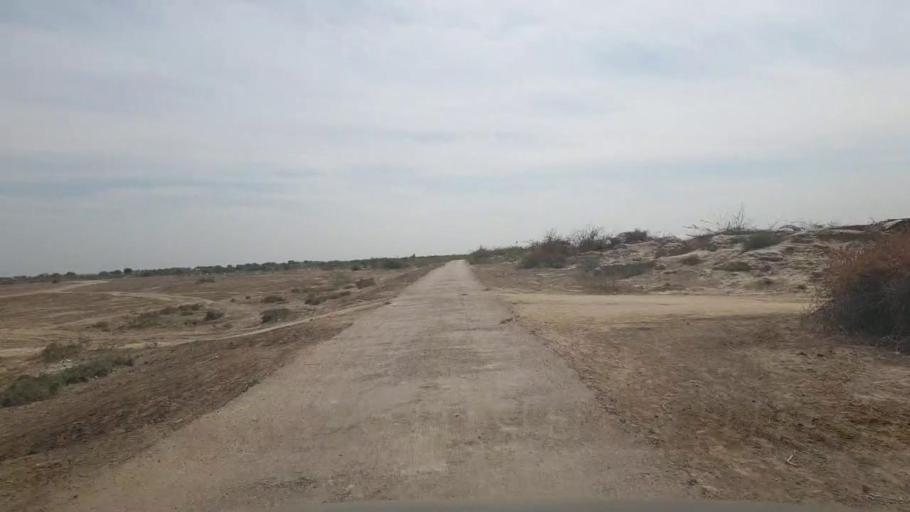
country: PK
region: Sindh
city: Kunri
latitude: 25.2647
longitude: 69.6032
